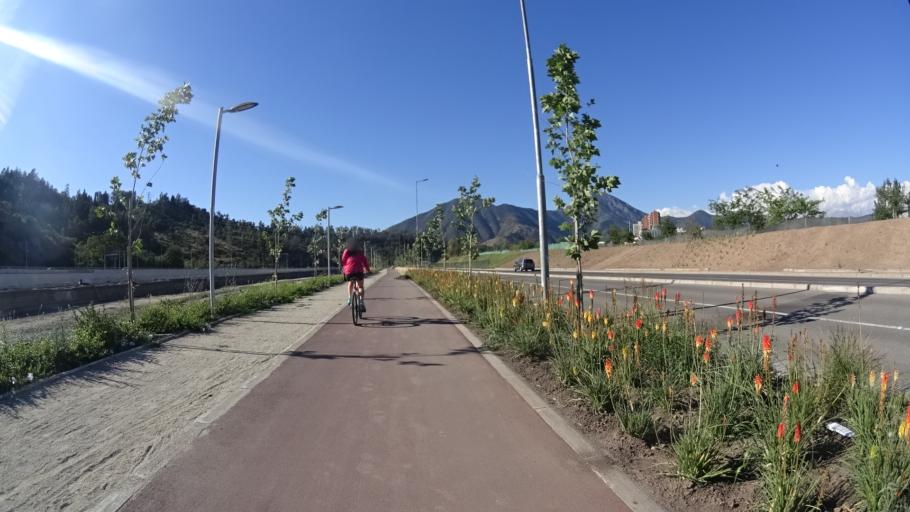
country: CL
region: Santiago Metropolitan
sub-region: Provincia de Santiago
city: Villa Presidente Frei, Nunoa, Santiago, Chile
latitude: -33.4028
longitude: -70.6030
